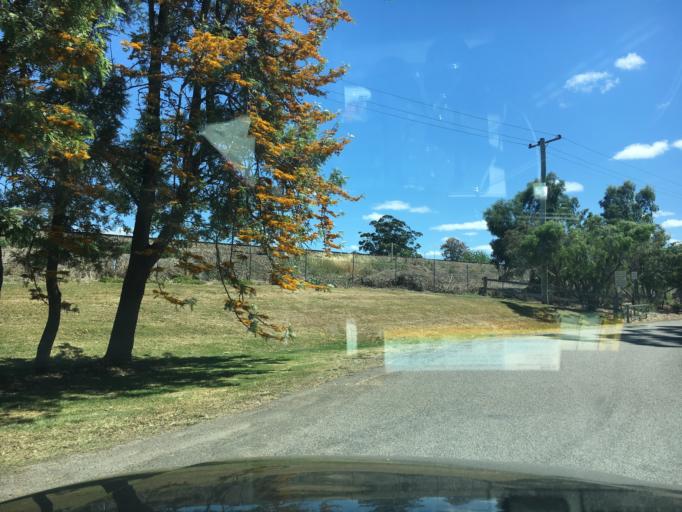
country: AU
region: New South Wales
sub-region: Singleton
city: Singleton
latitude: -32.5681
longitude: 151.1614
